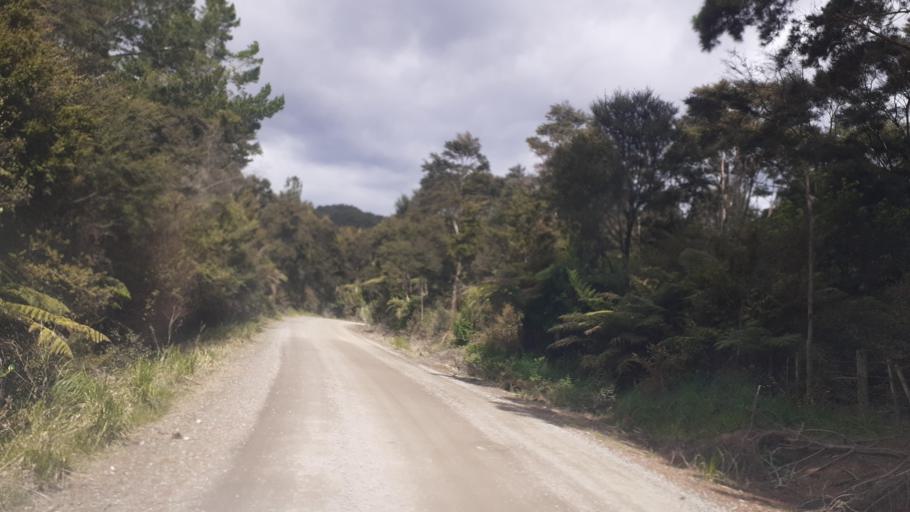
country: NZ
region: Northland
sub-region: Far North District
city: Moerewa
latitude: -35.5820
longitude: 173.9417
